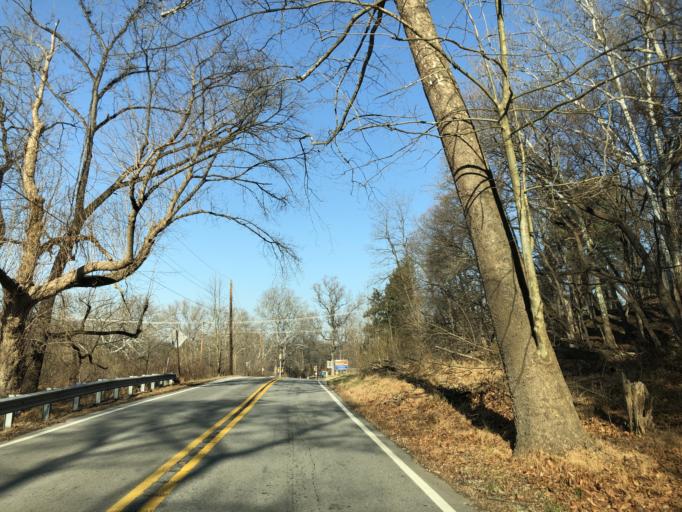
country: US
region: Pennsylvania
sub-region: Chester County
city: Chesterbrook
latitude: 40.0986
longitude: -75.4616
